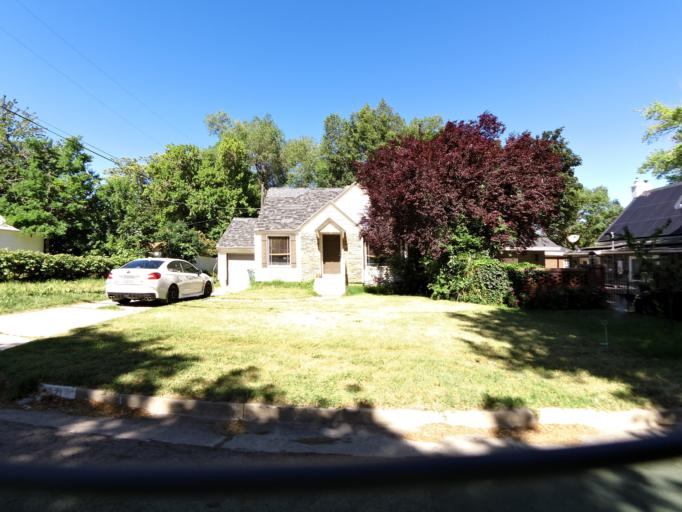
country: US
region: Utah
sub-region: Weber County
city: Ogden
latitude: 41.2157
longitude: -111.9456
